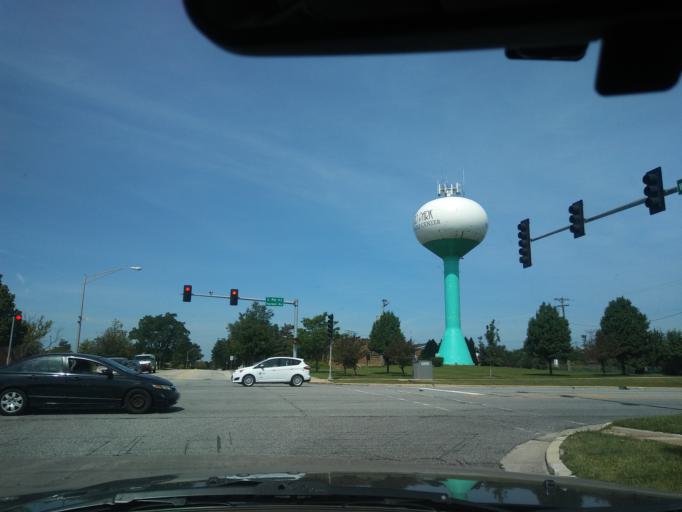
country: US
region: Illinois
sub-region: Cook County
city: Tinley Park
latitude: 41.6093
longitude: -87.7941
